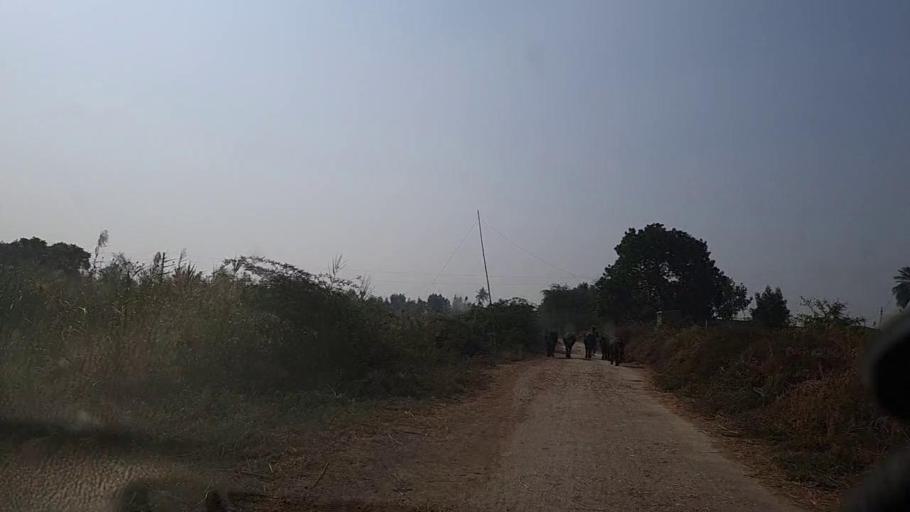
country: PK
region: Sindh
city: Thatta
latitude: 24.6522
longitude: 67.9099
